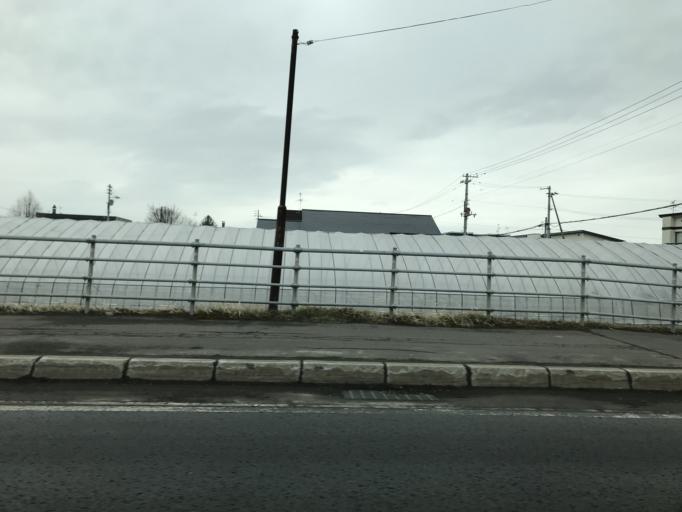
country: JP
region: Hokkaido
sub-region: Asahikawa-shi
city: Asahikawa
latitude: 43.8261
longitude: 142.4176
